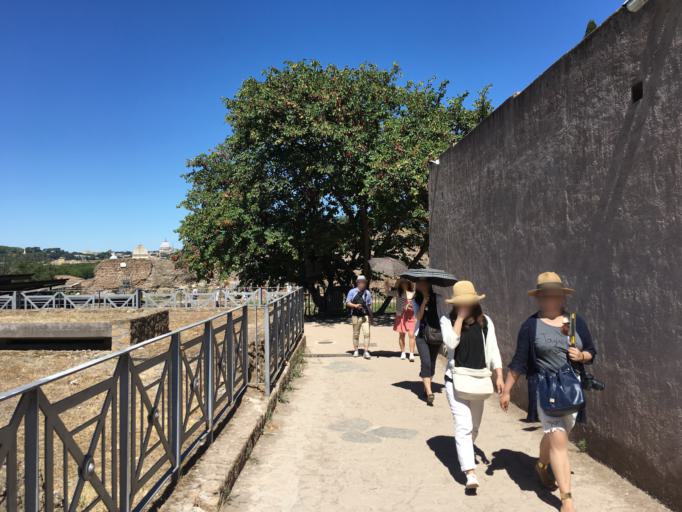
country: IT
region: Latium
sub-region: Citta metropolitana di Roma Capitale
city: Rome
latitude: 41.8892
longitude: 12.4856
